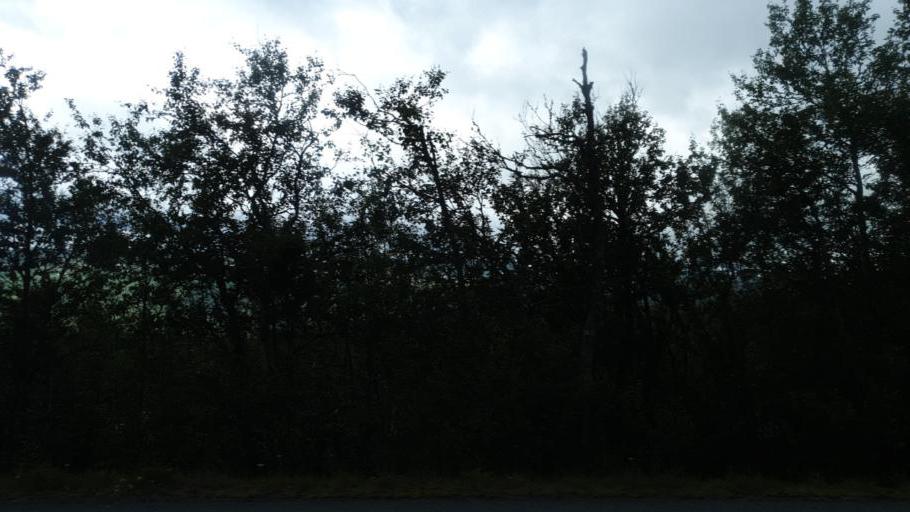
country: NO
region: Oppland
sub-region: Vestre Slidre
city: Slidre
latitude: 61.2553
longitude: 8.8766
